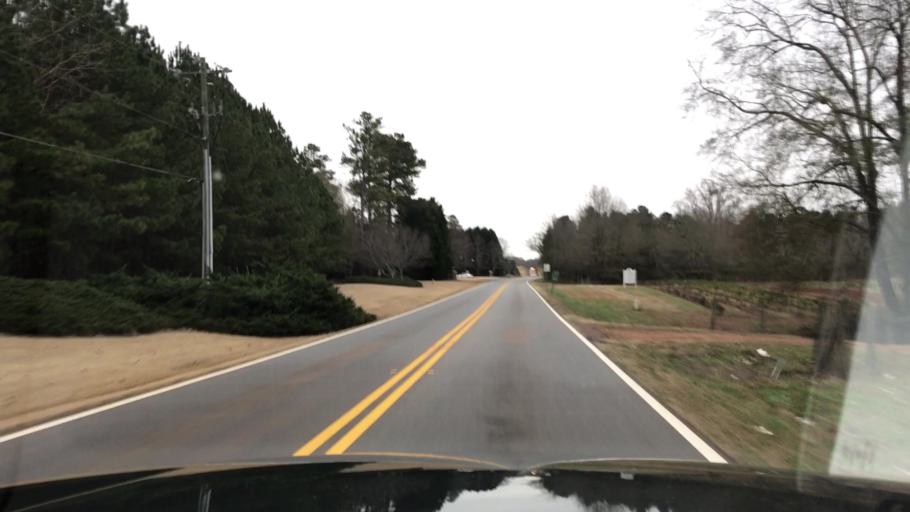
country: US
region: Georgia
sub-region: Walton County
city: Monroe
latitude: 33.8911
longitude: -83.7819
